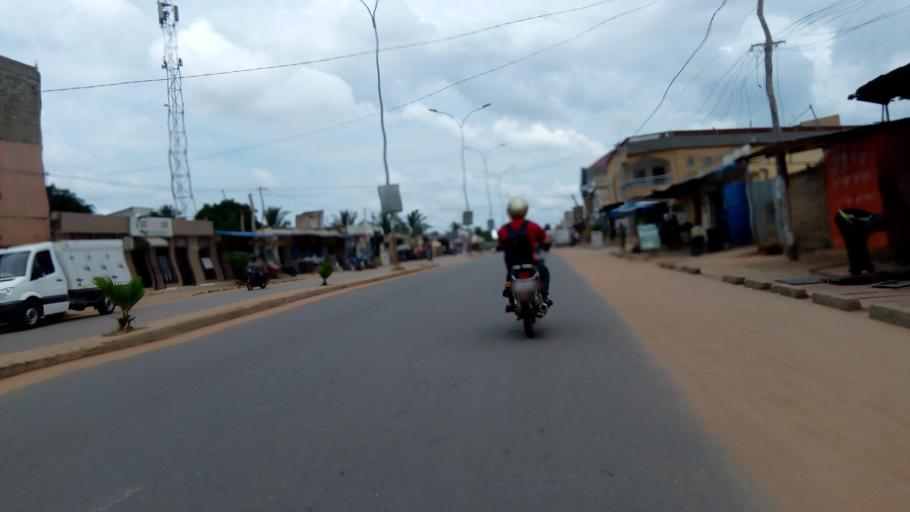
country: TG
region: Maritime
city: Lome
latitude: 6.2136
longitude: 1.1748
